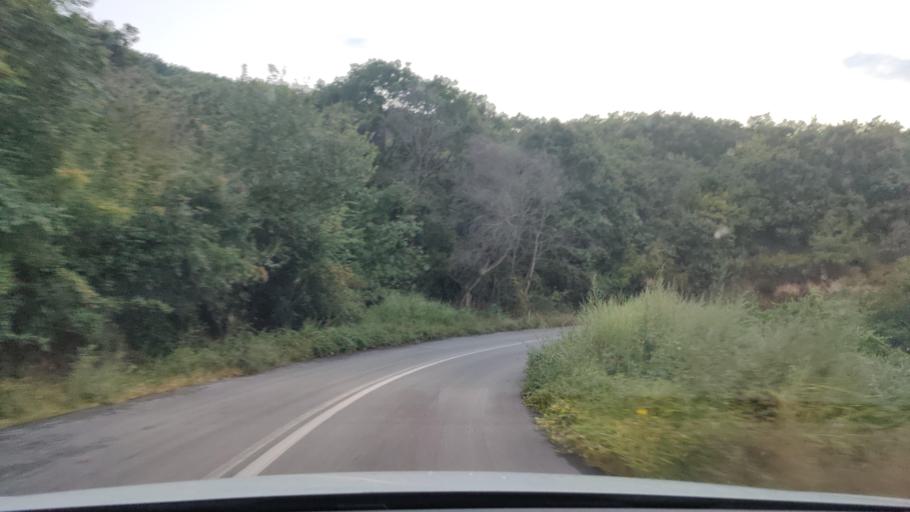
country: GR
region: Central Macedonia
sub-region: Nomos Serron
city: Chrysochorafa
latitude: 41.1768
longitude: 23.1669
